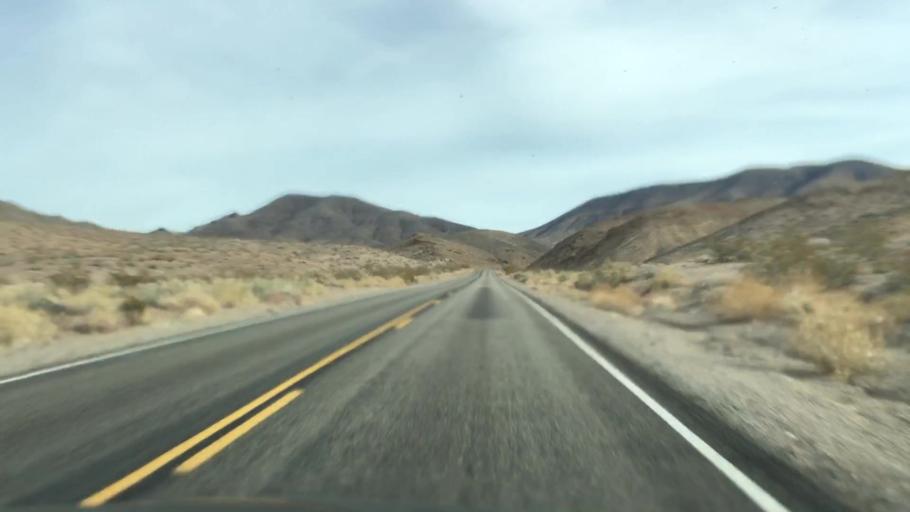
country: US
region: Nevada
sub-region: Nye County
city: Beatty
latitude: 36.7475
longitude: -116.9406
